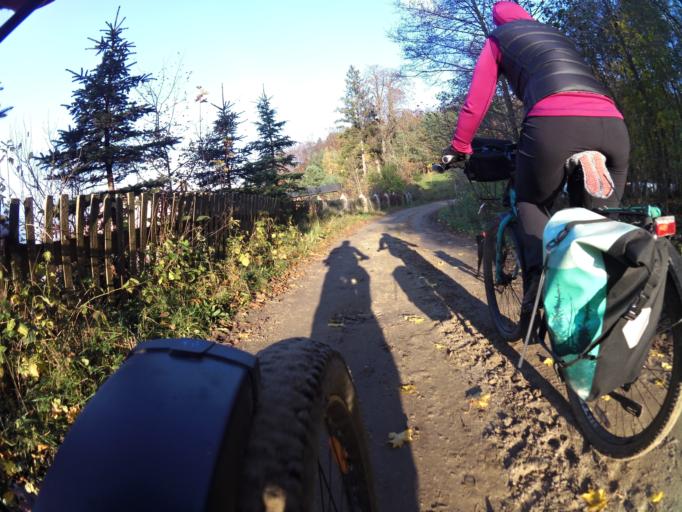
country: PL
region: Pomeranian Voivodeship
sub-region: Powiat pucki
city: Krokowa
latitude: 54.7463
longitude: 18.1951
